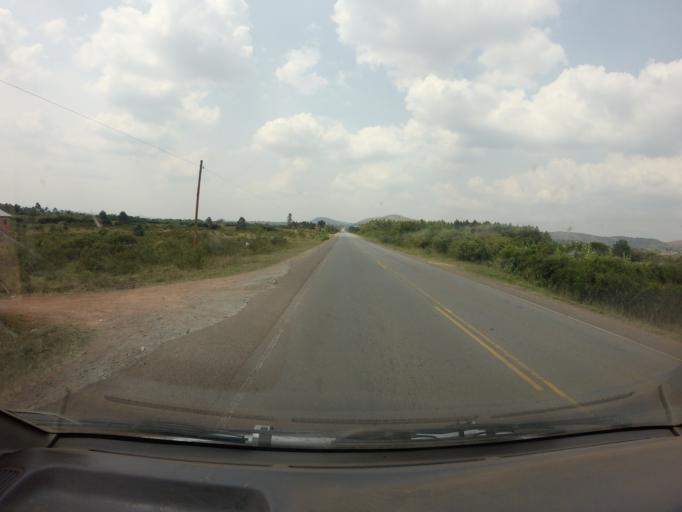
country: UG
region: Central Region
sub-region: Lyantonde District
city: Lyantonde
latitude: -0.3978
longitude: 31.1714
